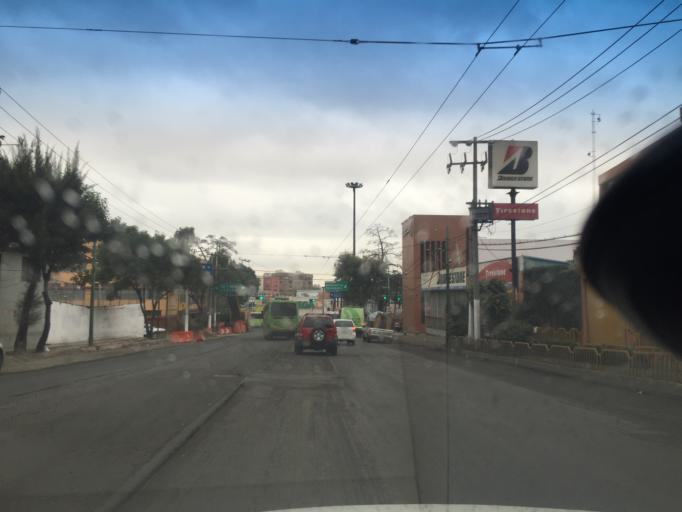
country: MX
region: Mexico City
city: Gustavo A. Madero
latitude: 19.4886
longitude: -99.1162
